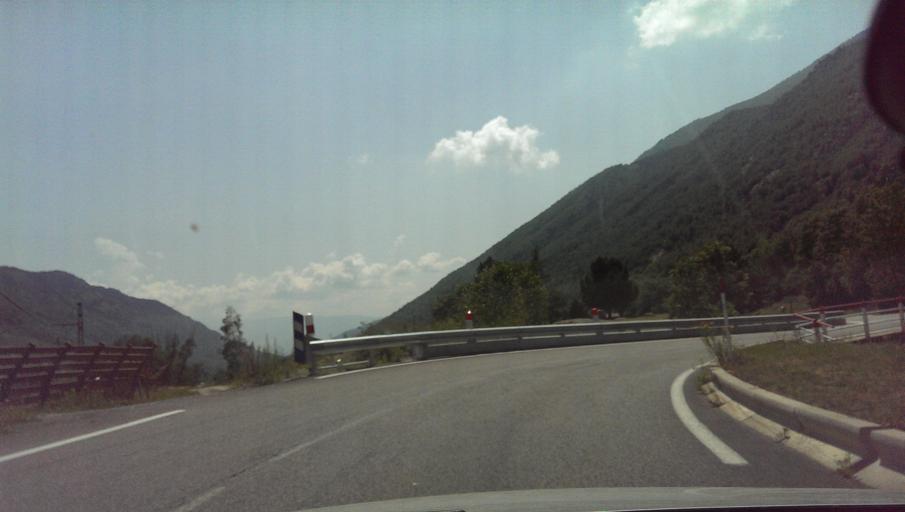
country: ES
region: Catalonia
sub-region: Provincia de Girona
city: Guils de Cerdanya
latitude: 42.5035
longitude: 1.8359
